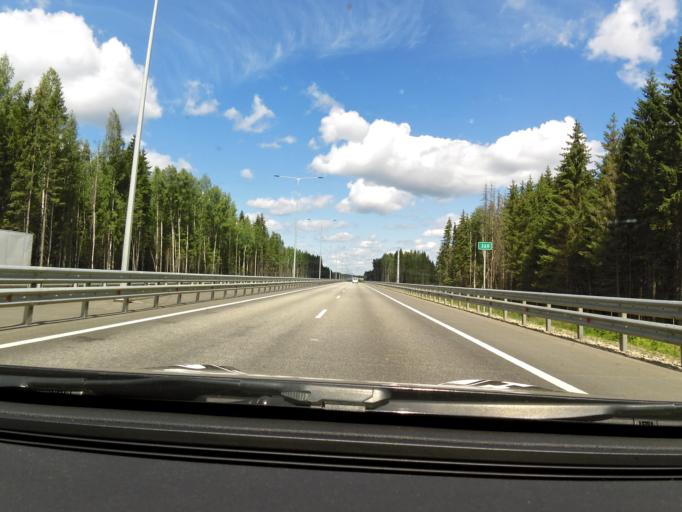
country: RU
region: Tverskaya
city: Krasnomayskiy
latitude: 57.6174
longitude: 34.2449
